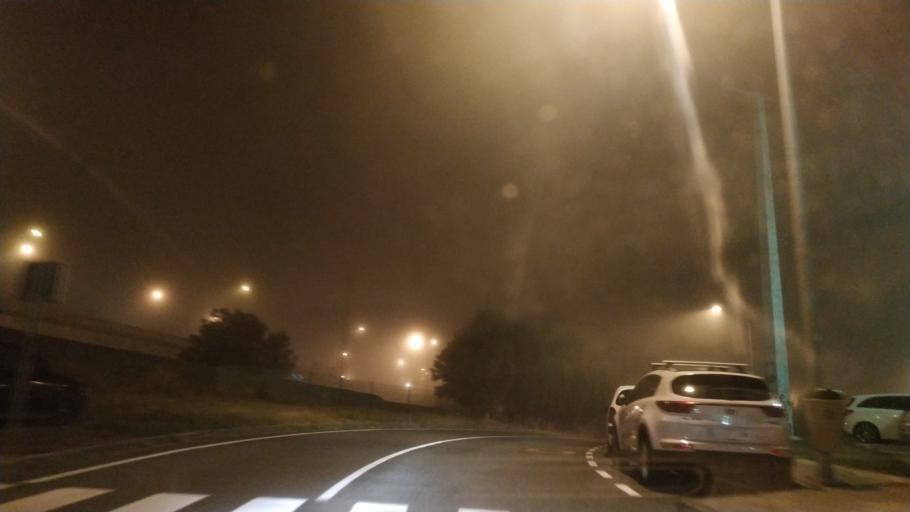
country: ES
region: Galicia
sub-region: Provincia da Coruna
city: Culleredo
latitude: 43.3287
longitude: -8.3960
